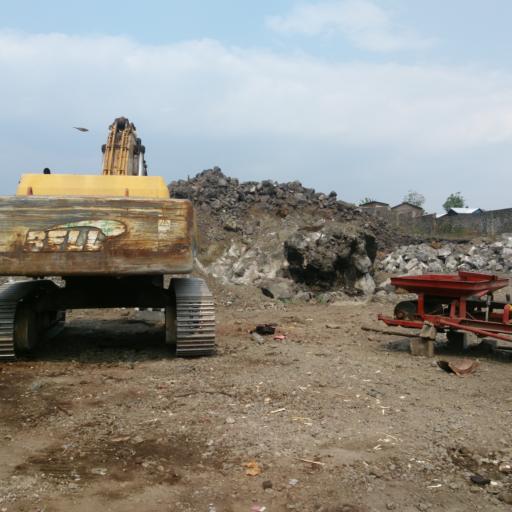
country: CD
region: Nord Kivu
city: Goma
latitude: -1.6465
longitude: 29.2445
